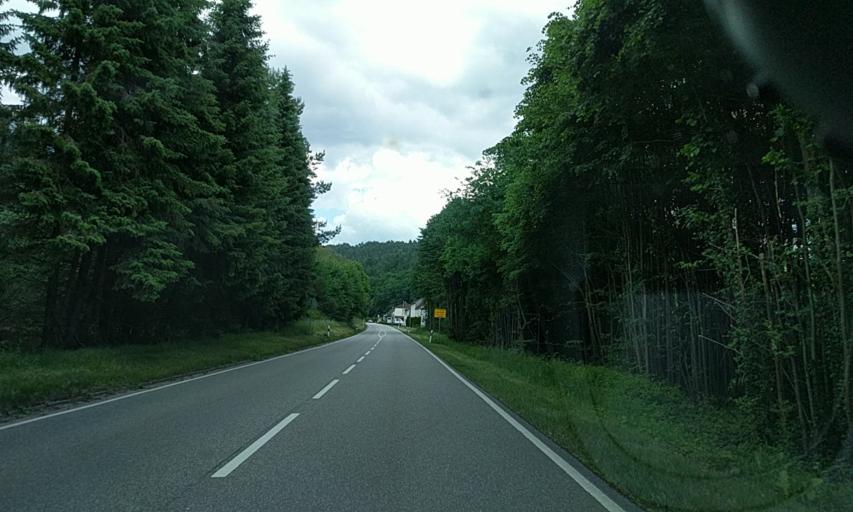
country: DE
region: Rheinland-Pfalz
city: Stelzenberg
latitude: 49.3963
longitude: 7.7101
